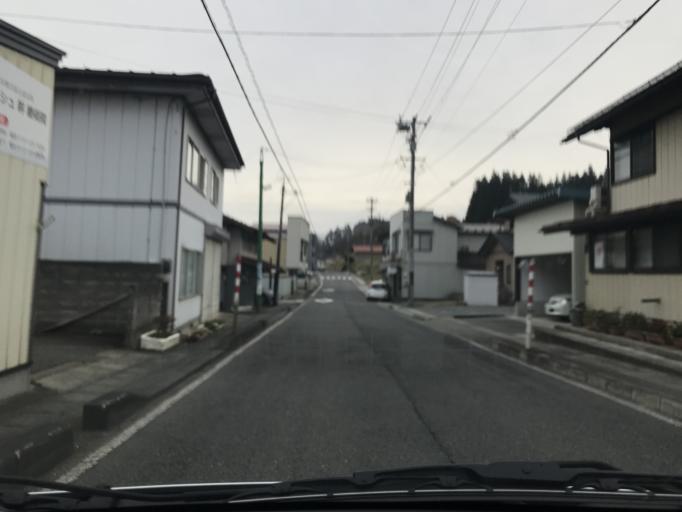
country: JP
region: Iwate
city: Kitakami
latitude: 39.2876
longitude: 141.2622
